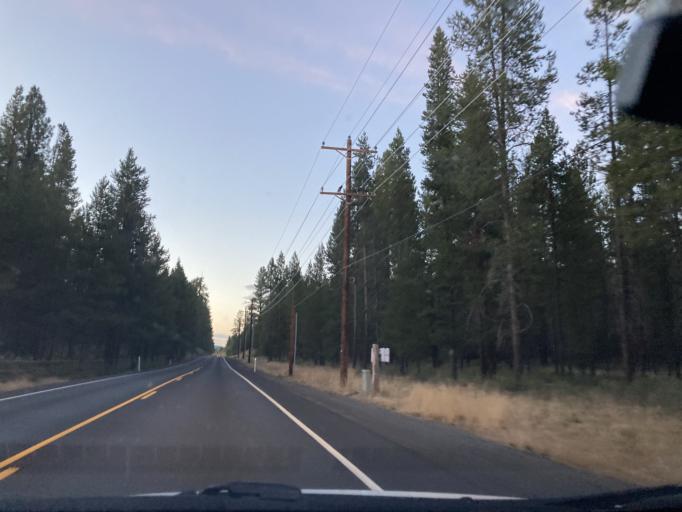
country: US
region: Oregon
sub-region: Deschutes County
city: Three Rivers
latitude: 43.8395
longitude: -121.4417
